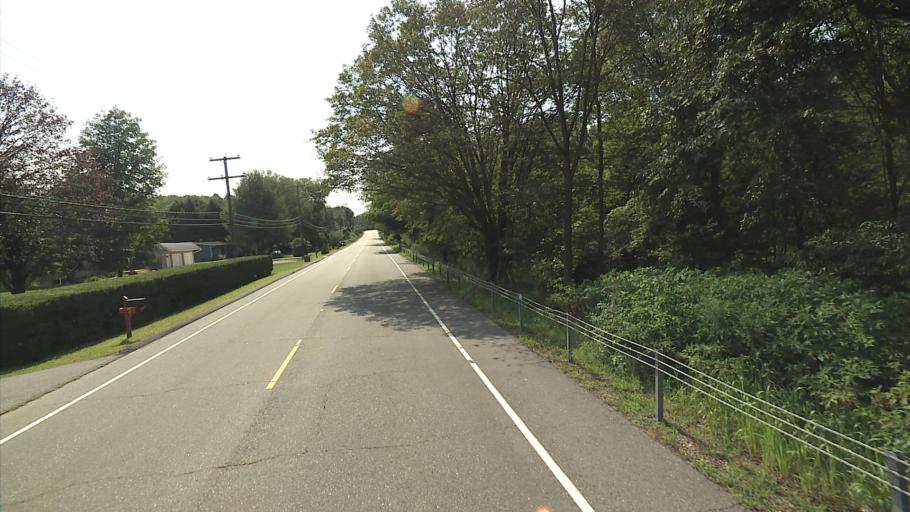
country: US
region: Connecticut
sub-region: New London County
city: Montville Center
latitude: 41.5682
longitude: -72.1727
